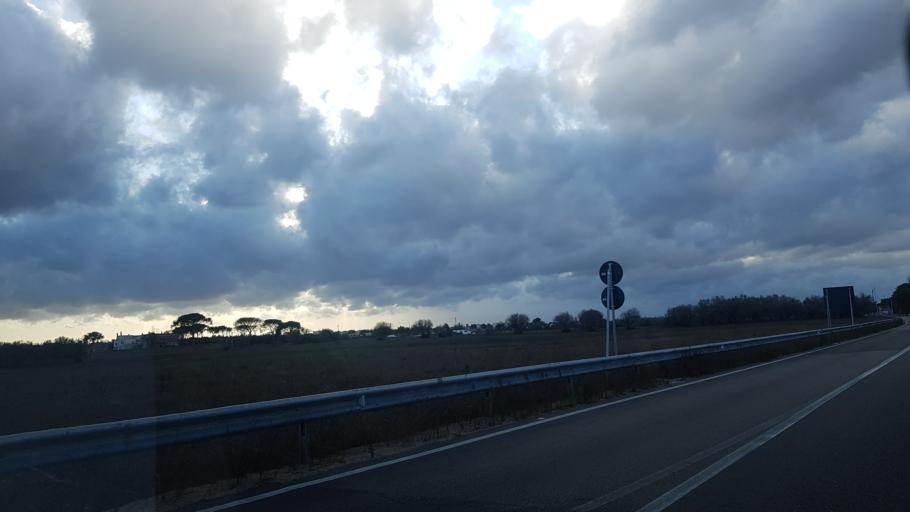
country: IT
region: Apulia
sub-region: Provincia di Brindisi
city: San Pietro Vernotico
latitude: 40.4873
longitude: 18.0198
